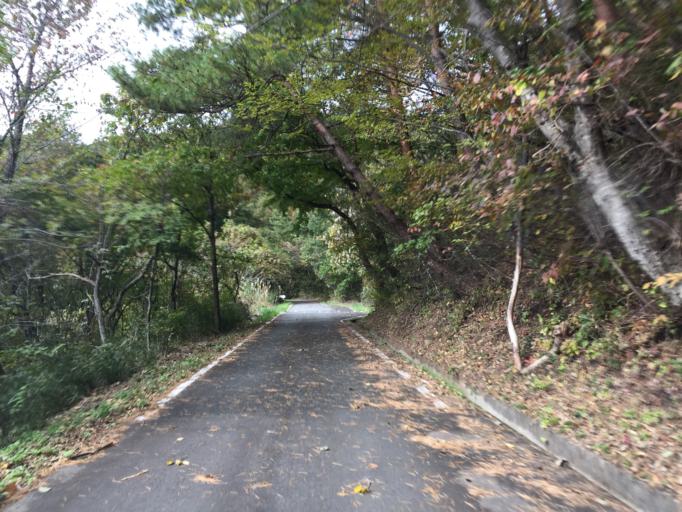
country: JP
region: Fukushima
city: Nihommatsu
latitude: 37.6768
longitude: 140.3834
